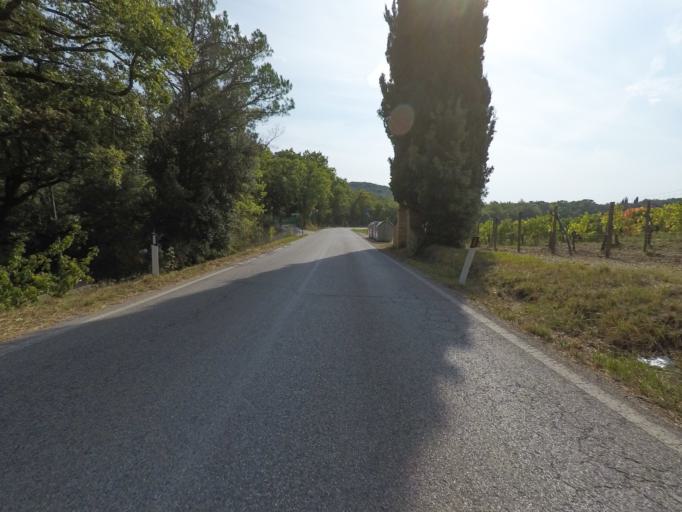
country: IT
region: Tuscany
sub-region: Provincia di Siena
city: Radda in Chianti
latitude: 43.4135
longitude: 11.3508
